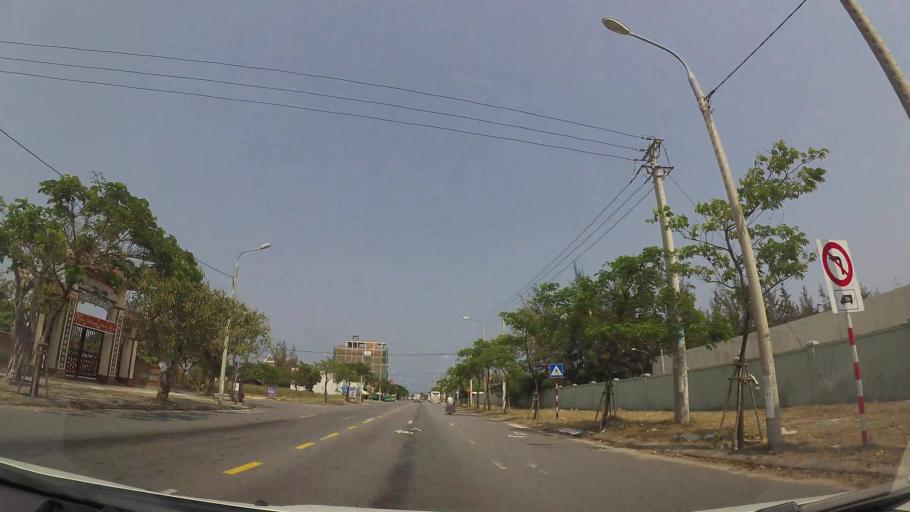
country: VN
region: Da Nang
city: Ngu Hanh Son
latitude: 15.9794
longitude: 108.2731
